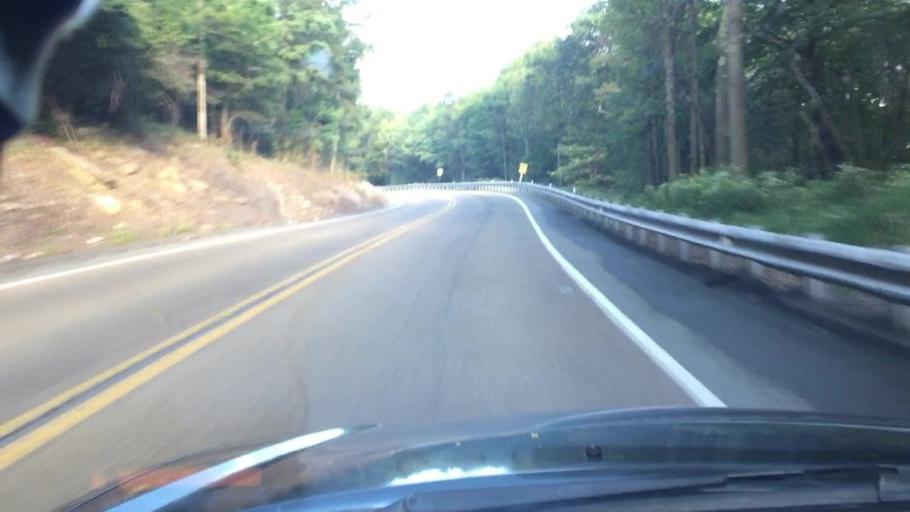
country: US
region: Pennsylvania
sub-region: Carbon County
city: Jim Thorpe
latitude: 40.8885
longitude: -75.7006
